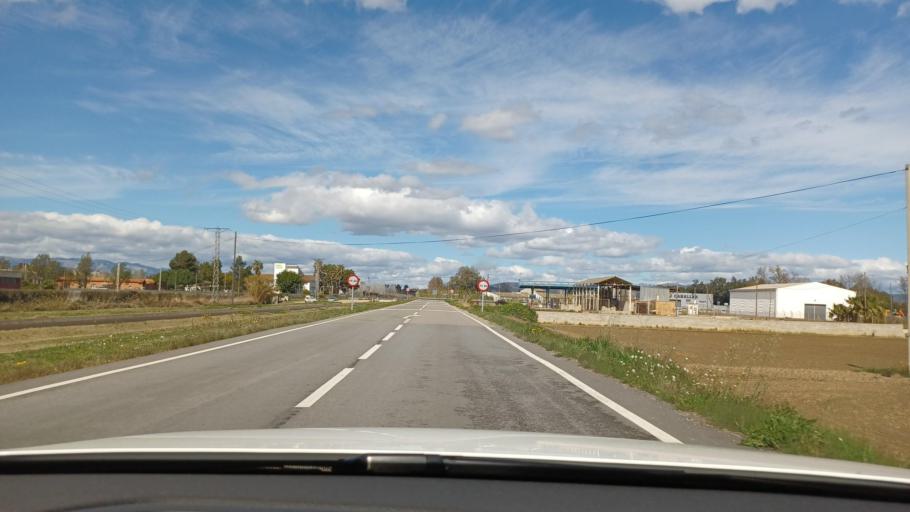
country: ES
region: Catalonia
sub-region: Provincia de Tarragona
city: Amposta
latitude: 40.7015
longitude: 0.5880
